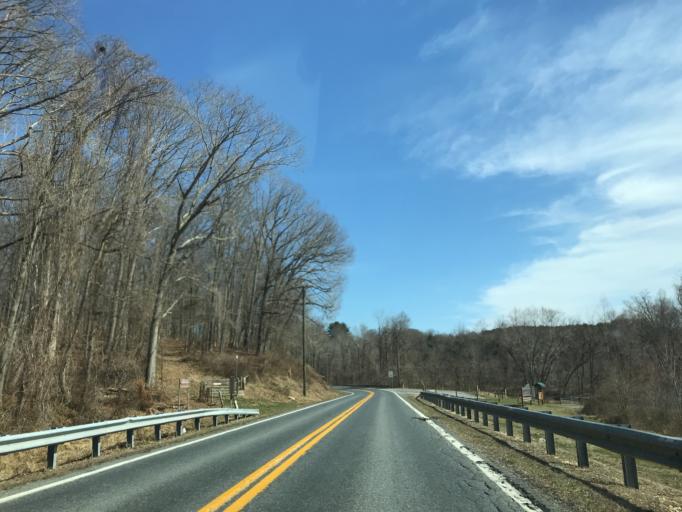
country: US
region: Maryland
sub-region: Howard County
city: Highland
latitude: 39.1464
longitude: -76.9616
